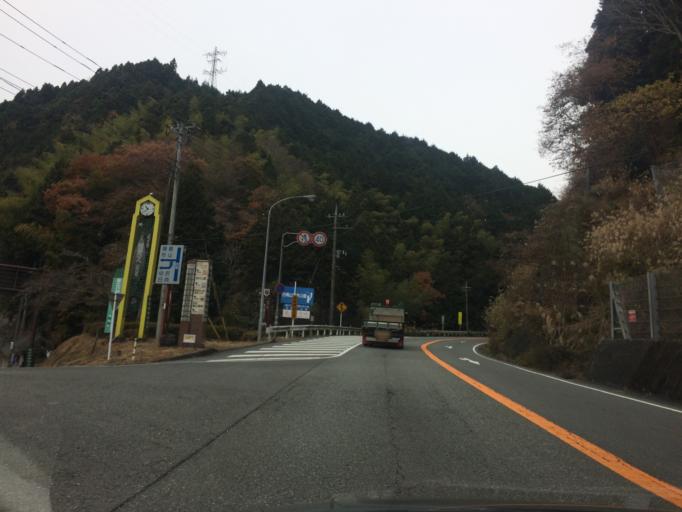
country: JP
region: Shizuoka
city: Fujinomiya
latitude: 35.1994
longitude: 138.5226
